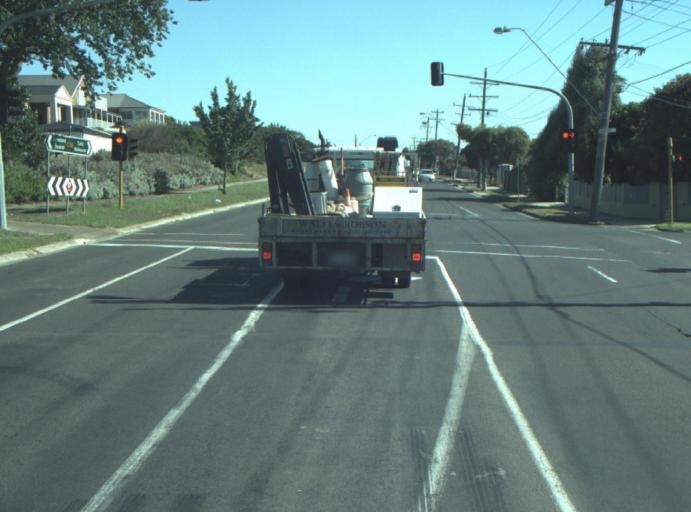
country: AU
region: Victoria
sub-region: Greater Geelong
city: Bell Park
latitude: -38.1097
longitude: 144.3317
